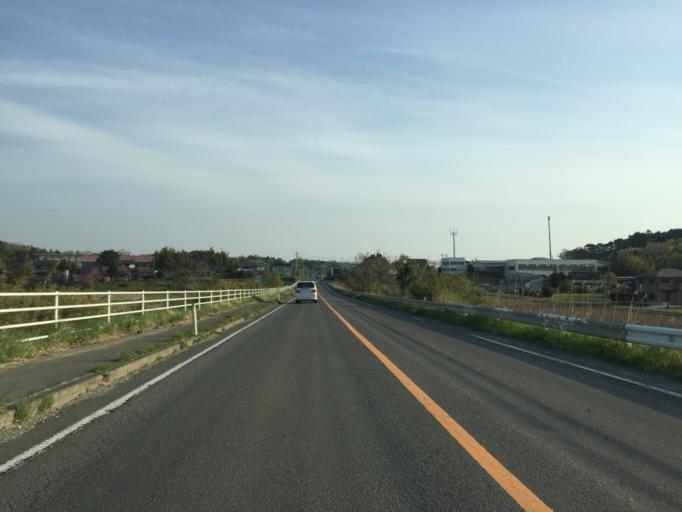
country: JP
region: Miyagi
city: Watari
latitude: 37.9374
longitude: 140.8941
